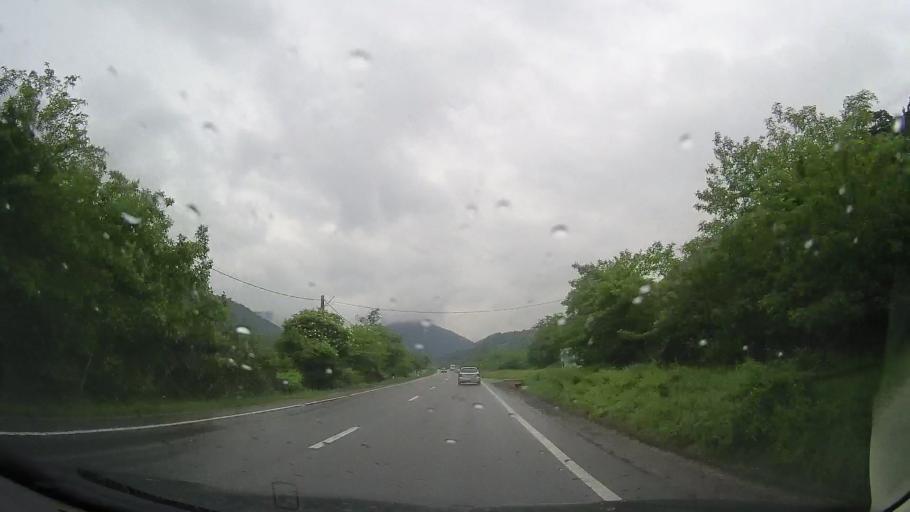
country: RO
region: Caras-Severin
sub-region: Comuna Mehadia
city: Mehadia
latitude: 44.8794
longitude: 22.3840
